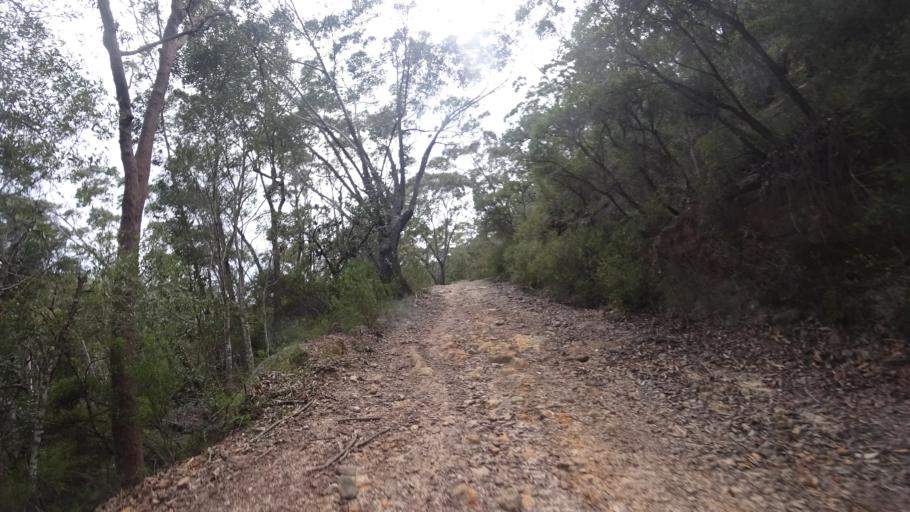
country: AU
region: New South Wales
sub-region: City of Sydney
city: North Turramurra
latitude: -33.6834
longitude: 151.1927
